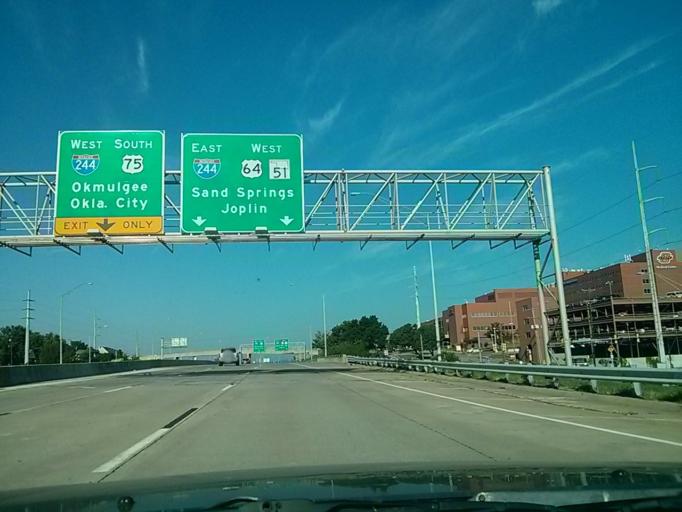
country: US
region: Oklahoma
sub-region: Tulsa County
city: Tulsa
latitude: 36.1456
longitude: -95.9970
